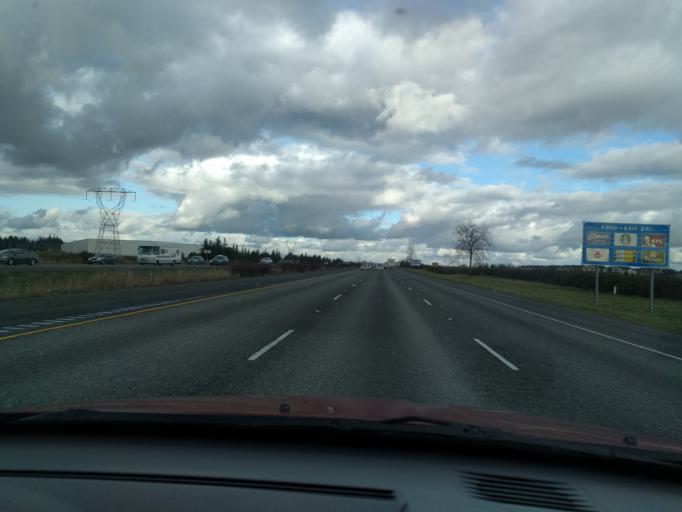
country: US
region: Oregon
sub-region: Marion County
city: Gervais
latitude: 45.1389
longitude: -122.8930
